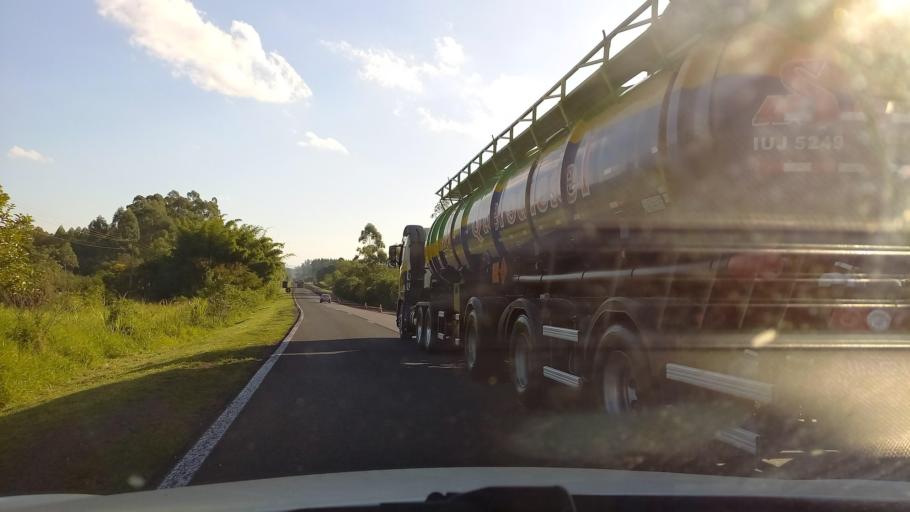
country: BR
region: Rio Grande do Sul
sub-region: Taquari
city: Taquari
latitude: -29.6982
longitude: -51.8339
